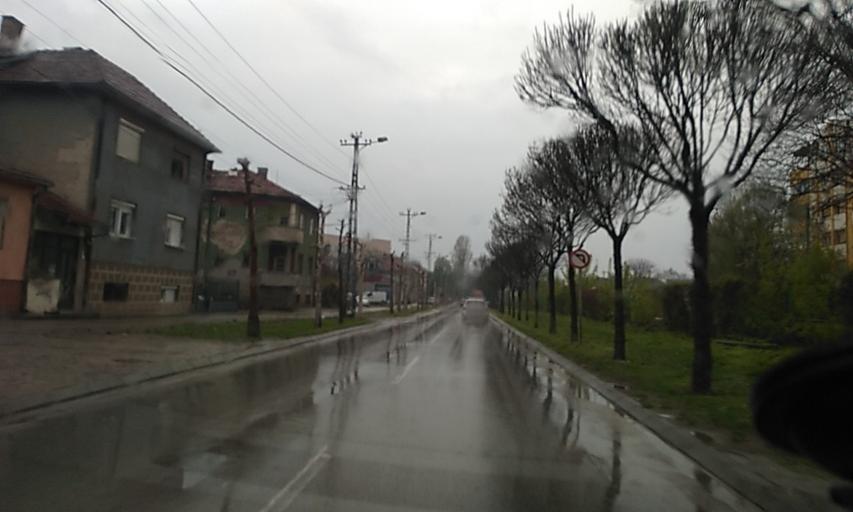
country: RS
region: Central Serbia
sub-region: Nisavski Okrug
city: Nis
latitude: 43.3143
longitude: 21.8861
